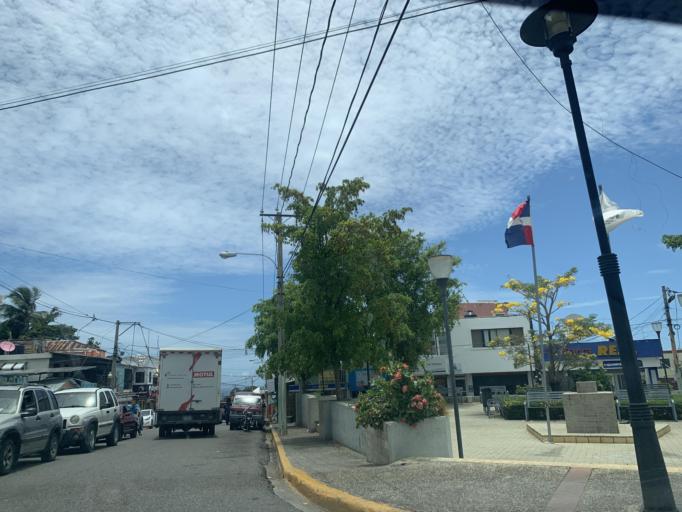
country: DO
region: Puerto Plata
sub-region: Puerto Plata
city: Puerto Plata
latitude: 19.7861
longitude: -70.6881
